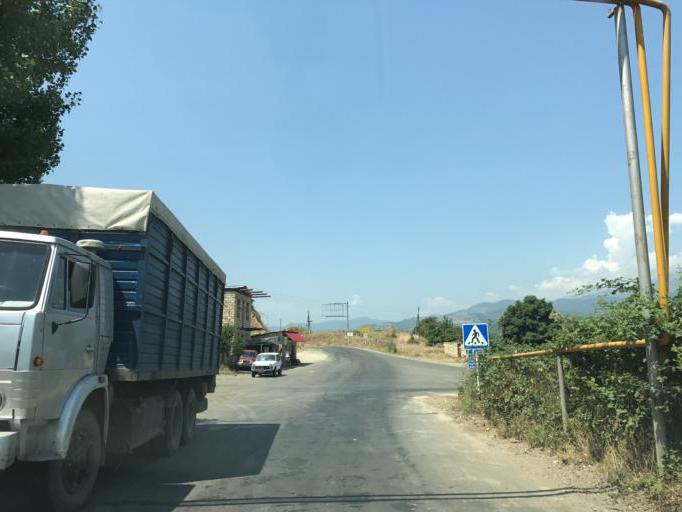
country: AZ
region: Tartar Rayon
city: Martakert
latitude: 40.1462
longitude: 46.6031
